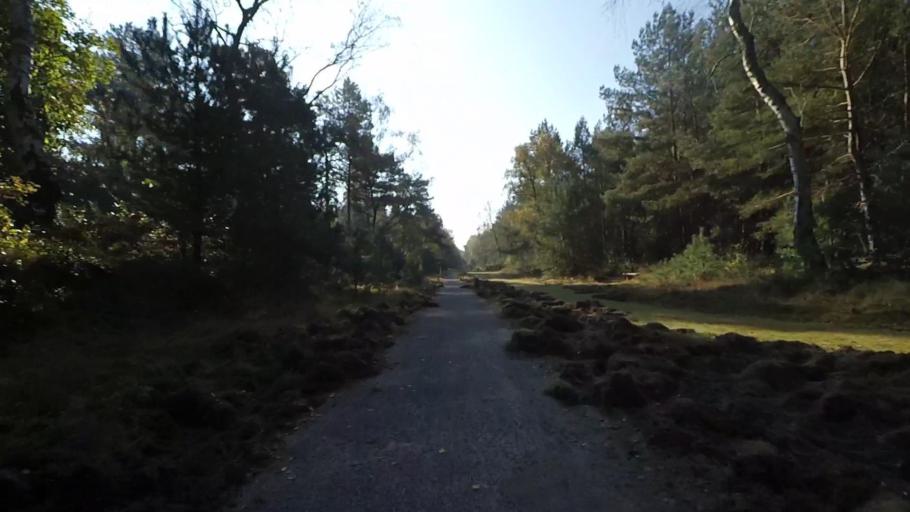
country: NL
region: Gelderland
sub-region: Gemeente Harderwijk
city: Harderwijk
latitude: 52.3278
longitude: 5.6536
